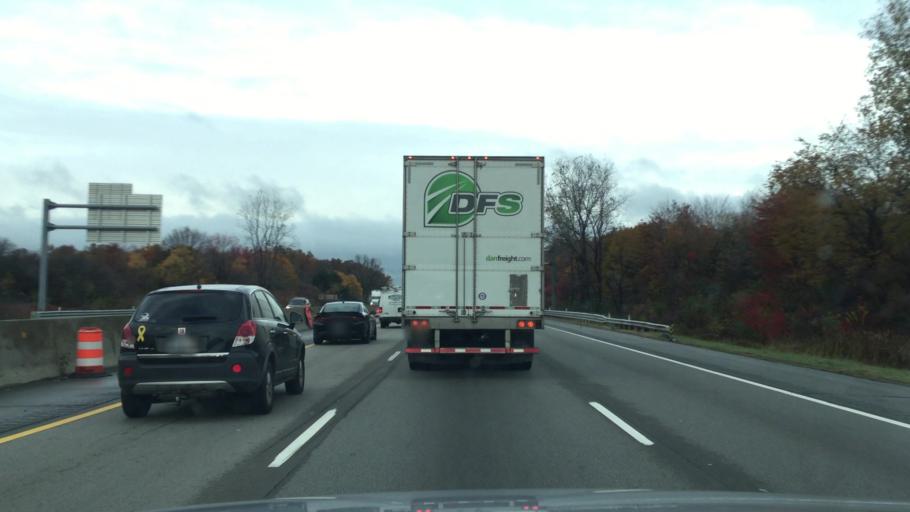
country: US
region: Michigan
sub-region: Washtenaw County
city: Ypsilanti
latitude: 42.2248
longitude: -83.6707
